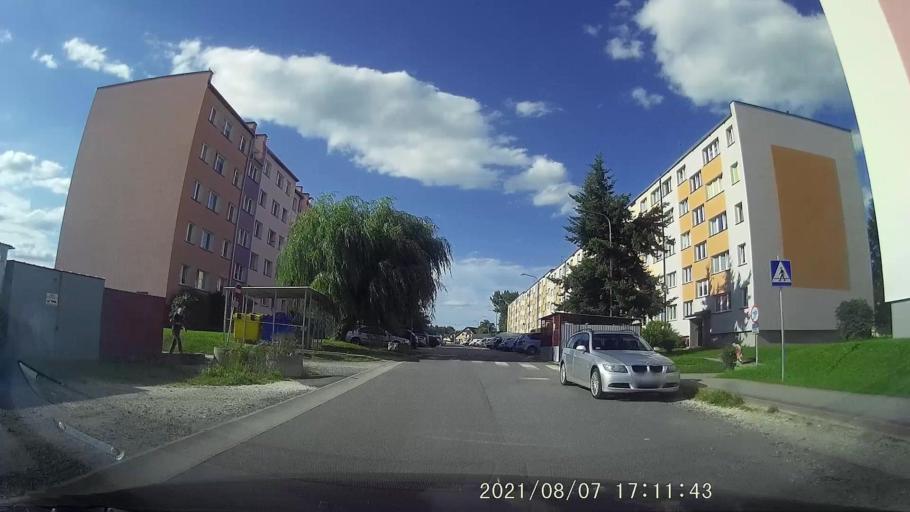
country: PL
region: Lower Silesian Voivodeship
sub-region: Powiat klodzki
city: Bystrzyca Klodzka
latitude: 50.3021
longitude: 16.6348
